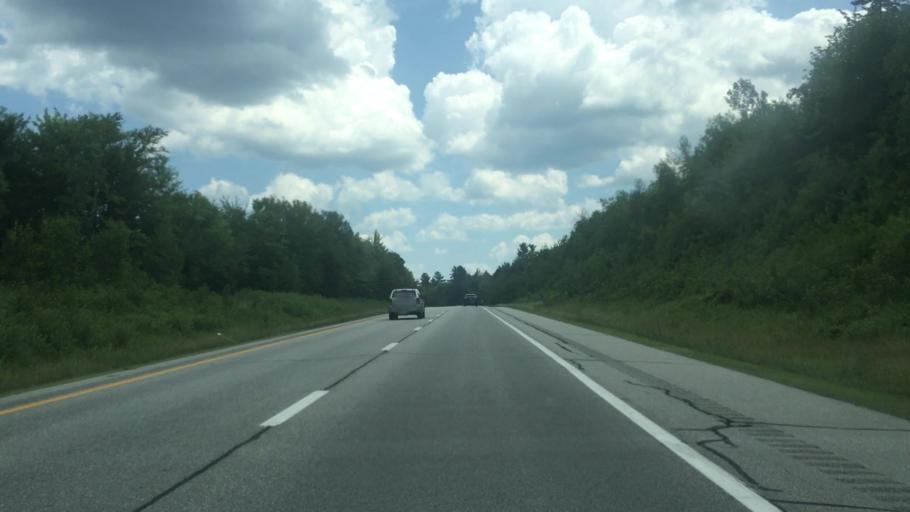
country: US
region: New Hampshire
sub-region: Merrimack County
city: New London
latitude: 43.3998
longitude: -72.0151
